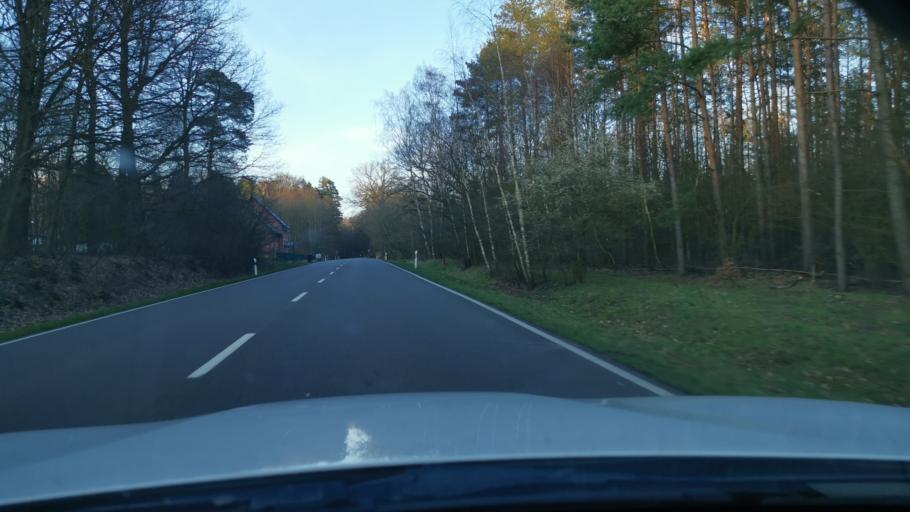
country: DE
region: Saxony
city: Bad Duben
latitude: 51.6609
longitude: 12.5970
